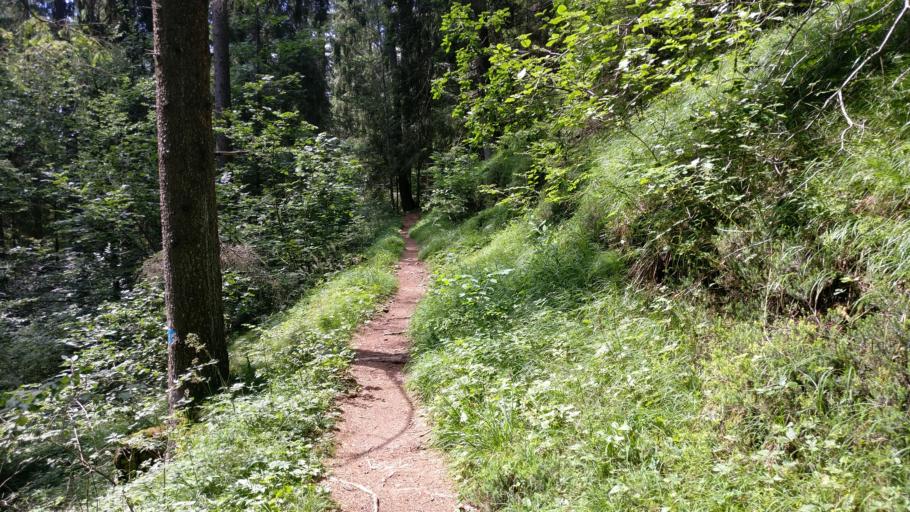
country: IT
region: Trentino-Alto Adige
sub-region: Provincia di Trento
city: Ruffre
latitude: 46.4214
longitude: 11.1963
